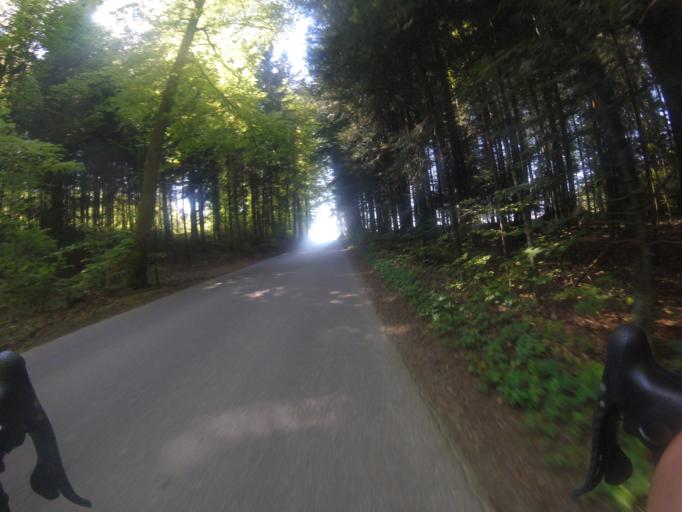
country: CH
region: Bern
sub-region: Bern-Mittelland District
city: Muhleberg
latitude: 46.9778
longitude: 7.2367
